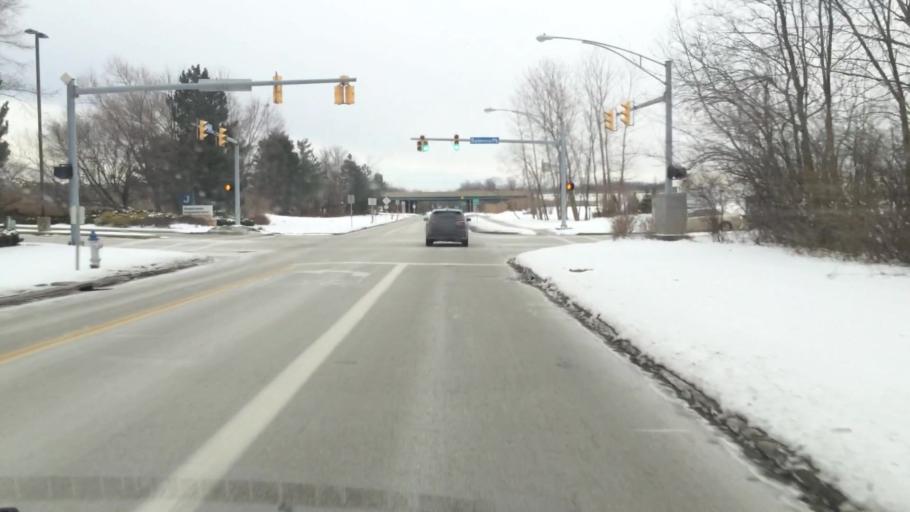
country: US
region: Ohio
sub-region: Cuyahoga County
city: Beachwood
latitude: 41.4736
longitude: -81.4919
